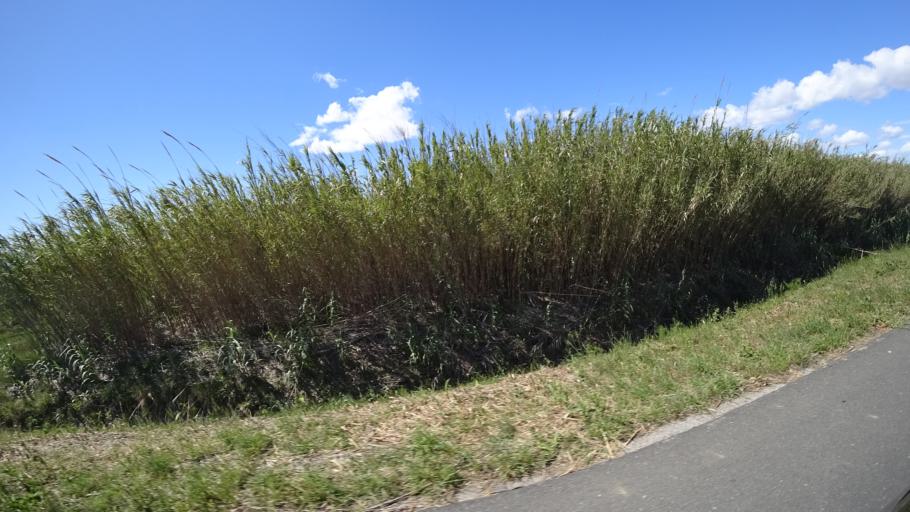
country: FR
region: Languedoc-Roussillon
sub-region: Departement des Pyrenees-Orientales
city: Saint-Nazaire
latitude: 42.6795
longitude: 2.9934
